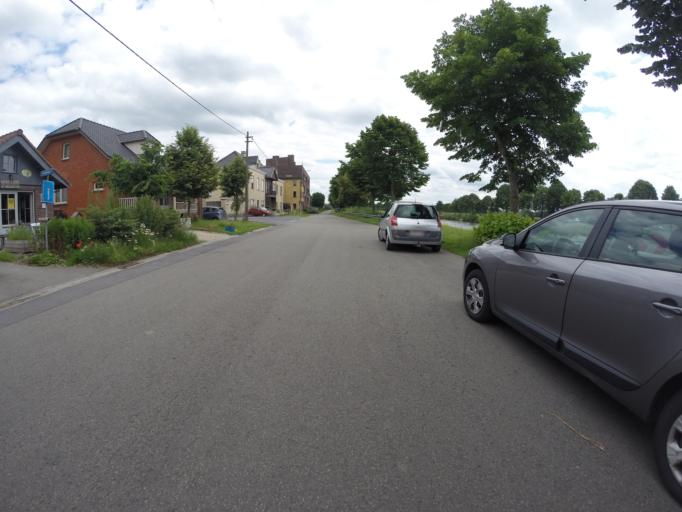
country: BE
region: Flanders
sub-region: Provincie Oost-Vlaanderen
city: Aalter
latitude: 51.0968
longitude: 3.4997
